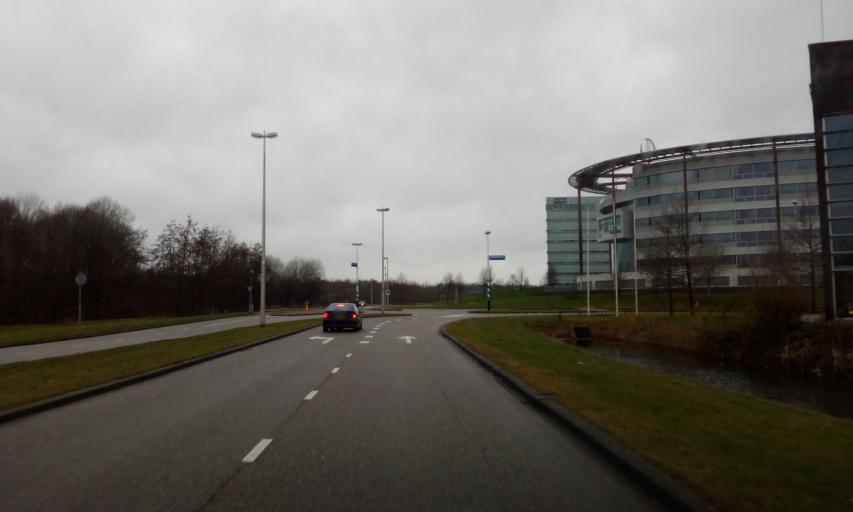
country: NL
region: Utrecht
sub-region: Gemeente Nieuwegein
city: Nieuwegein
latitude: 52.0654
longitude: 5.0789
